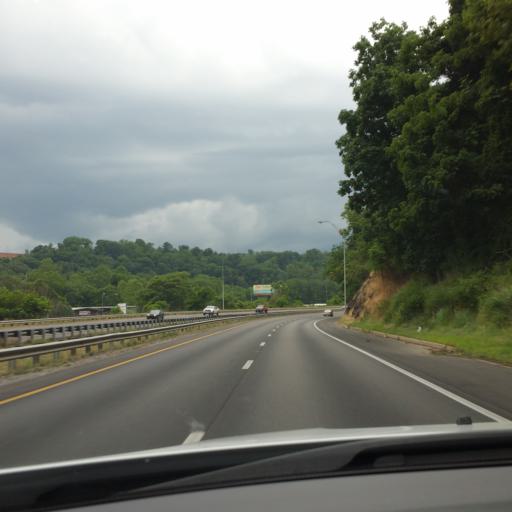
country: US
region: North Carolina
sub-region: Buncombe County
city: Asheville
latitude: 35.6025
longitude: -82.5753
